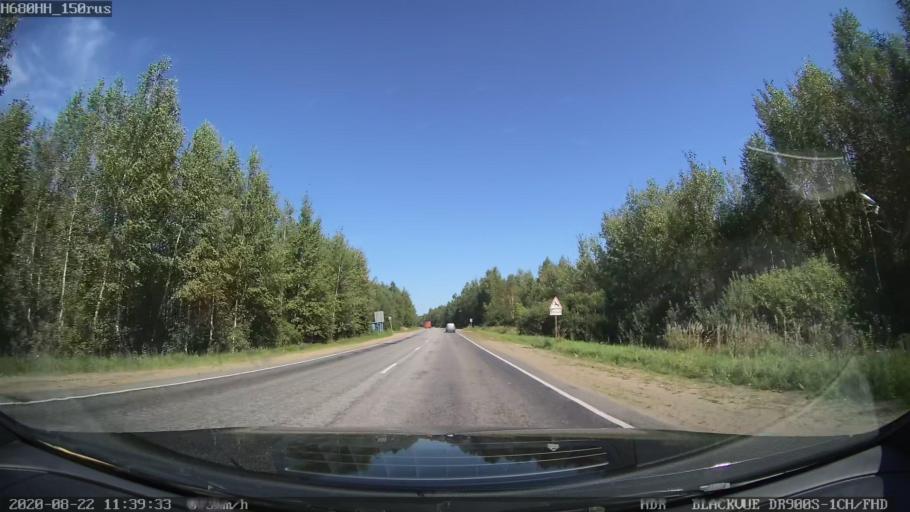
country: RU
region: Tverskaya
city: Sakharovo
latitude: 56.9663
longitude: 36.0221
